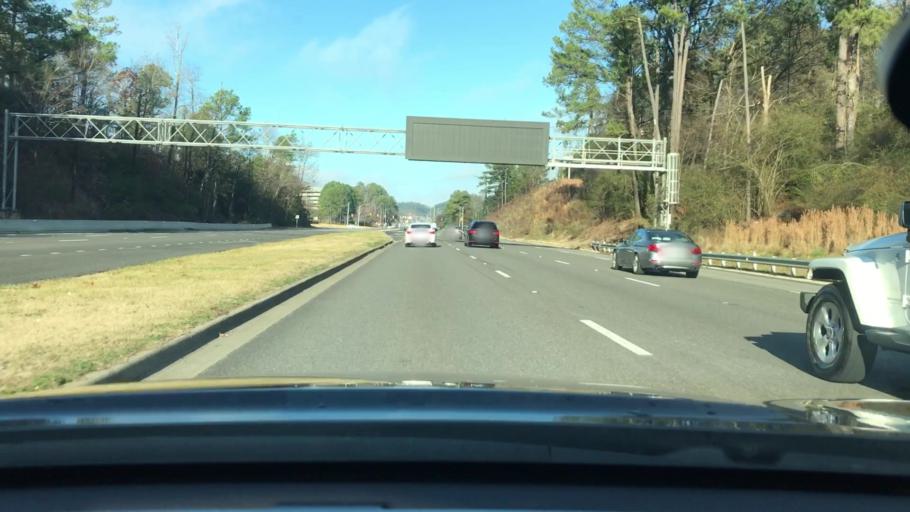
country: US
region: Alabama
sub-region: Jefferson County
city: Cahaba Heights
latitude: 33.4337
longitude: -86.7157
